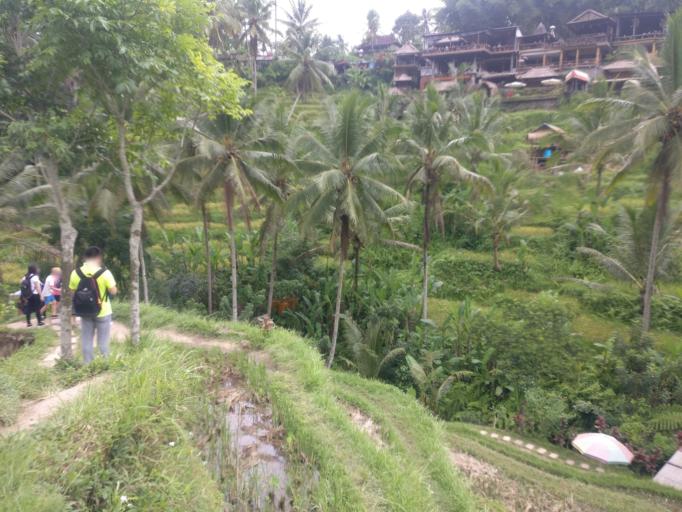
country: ID
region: Bali
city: Tegalalang
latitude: -8.4333
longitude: 115.2795
